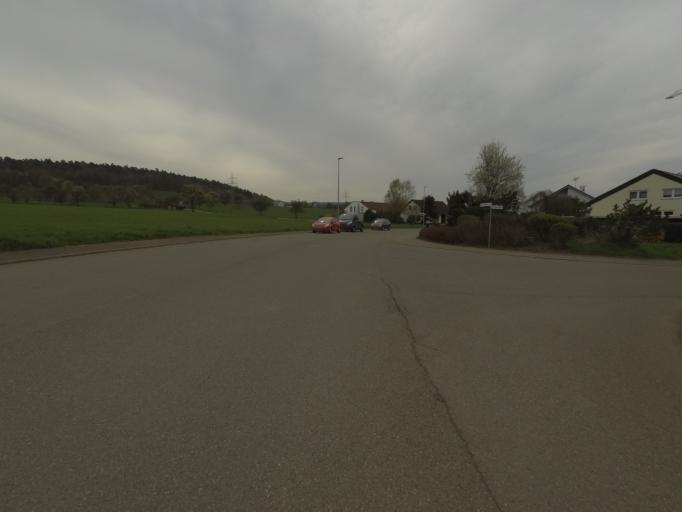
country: DE
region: Baden-Wuerttemberg
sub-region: Tuebingen Region
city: Gomaringen
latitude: 48.4524
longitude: 9.1092
